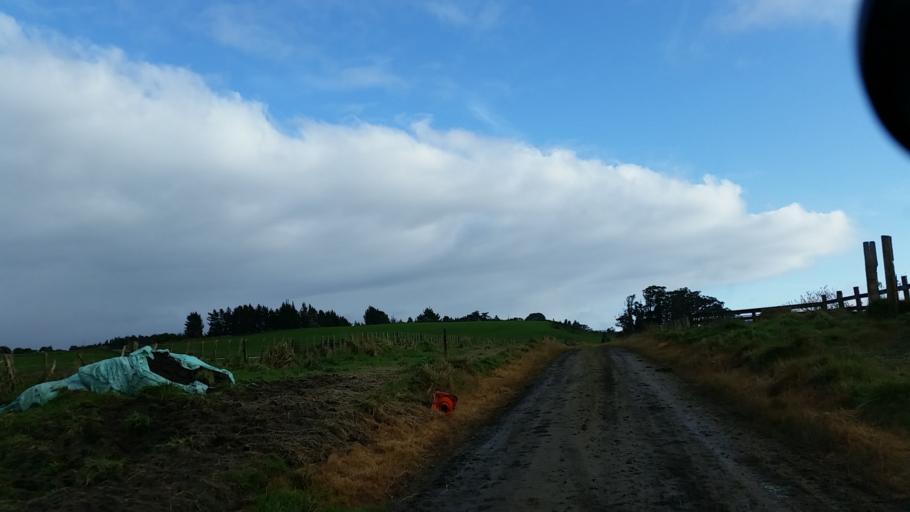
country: NZ
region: Taranaki
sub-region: South Taranaki District
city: Patea
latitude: -39.7257
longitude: 174.7215
